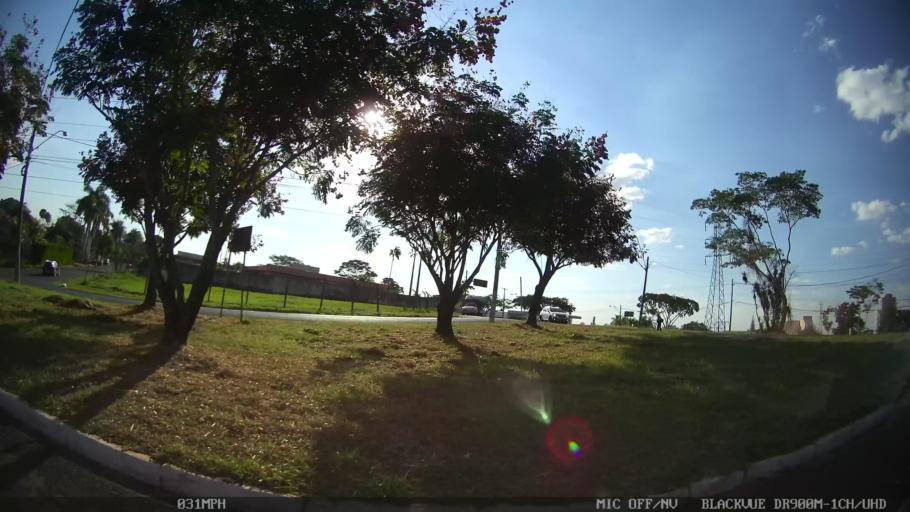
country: BR
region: Sao Paulo
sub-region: Ribeirao Preto
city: Ribeirao Preto
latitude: -21.2037
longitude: -47.7817
